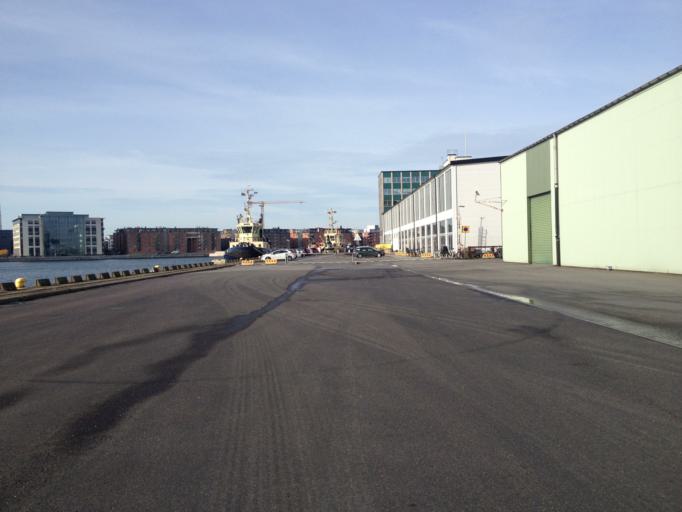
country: SE
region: Skane
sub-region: Malmo
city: Malmoe
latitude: 55.6156
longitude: 12.9992
